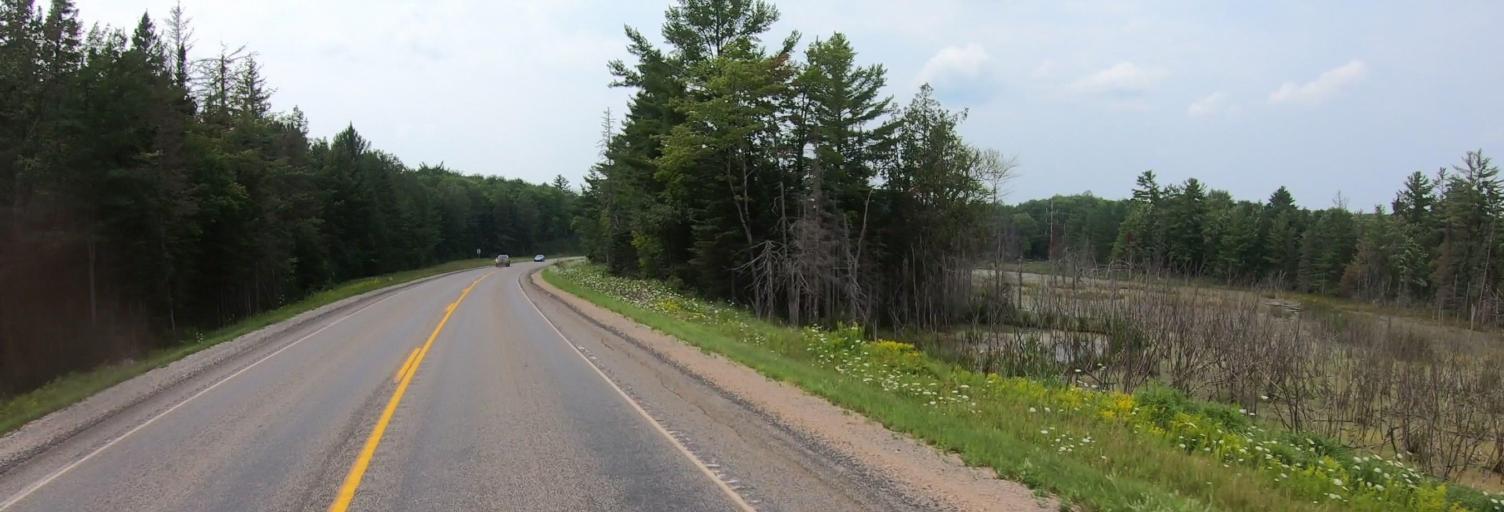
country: US
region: Michigan
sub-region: Alger County
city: Munising
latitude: 46.3329
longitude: -86.8255
